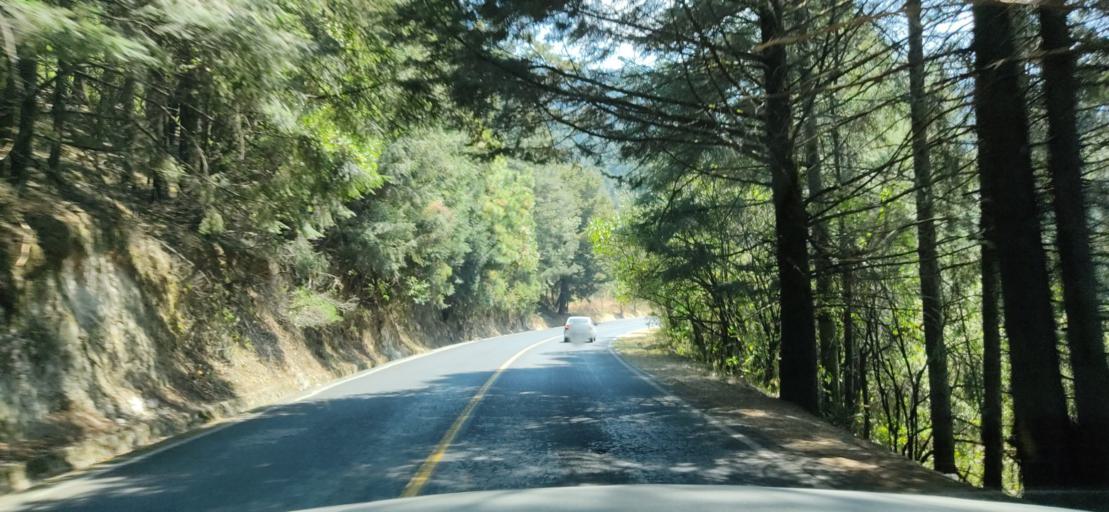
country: MX
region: Mexico
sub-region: Ocoyoacac
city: San Jeronimo Acazulco
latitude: 19.2511
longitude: -99.3736
